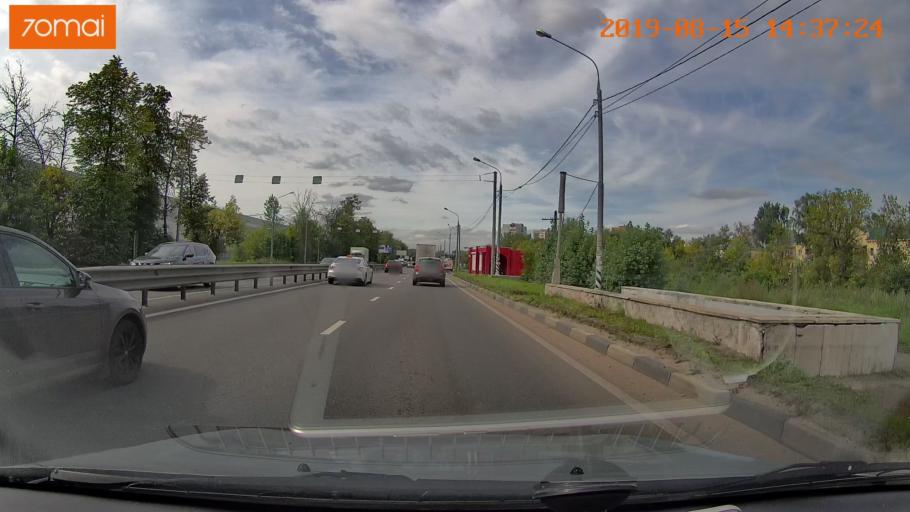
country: RU
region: Moskovskaya
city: Tomilino
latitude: 55.6525
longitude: 37.9270
